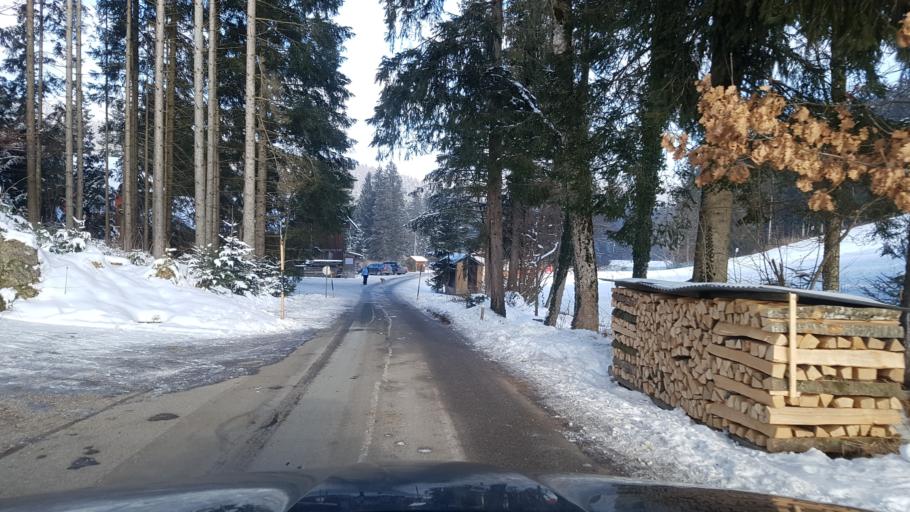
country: AT
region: Salzburg
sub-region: Politischer Bezirk Salzburg-Umgebung
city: Thalgau
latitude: 47.8658
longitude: 13.2539
